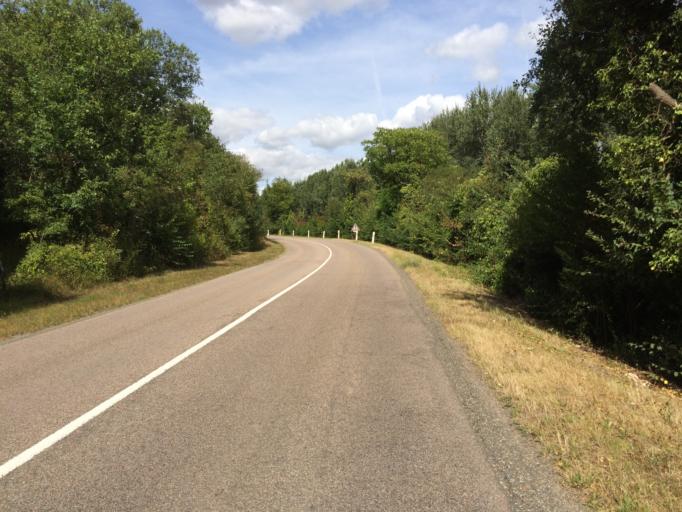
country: FR
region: Ile-de-France
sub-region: Departement de l'Essonne
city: Maisse
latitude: 48.3495
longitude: 2.3811
